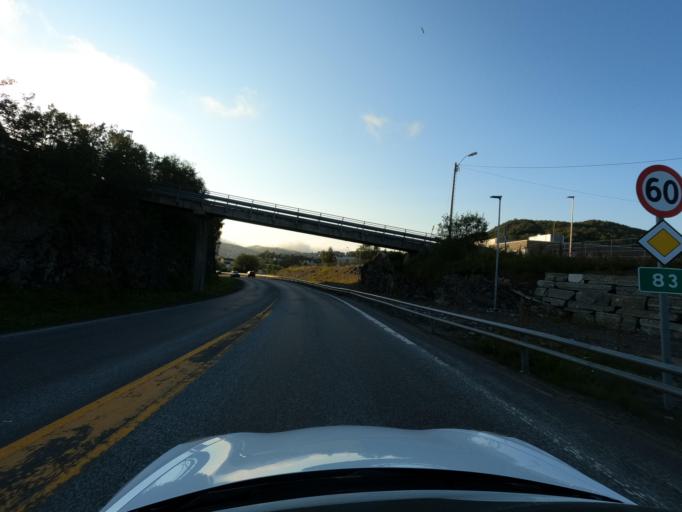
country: NO
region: Troms
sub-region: Harstad
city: Harstad
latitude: 68.7823
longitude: 16.5640
